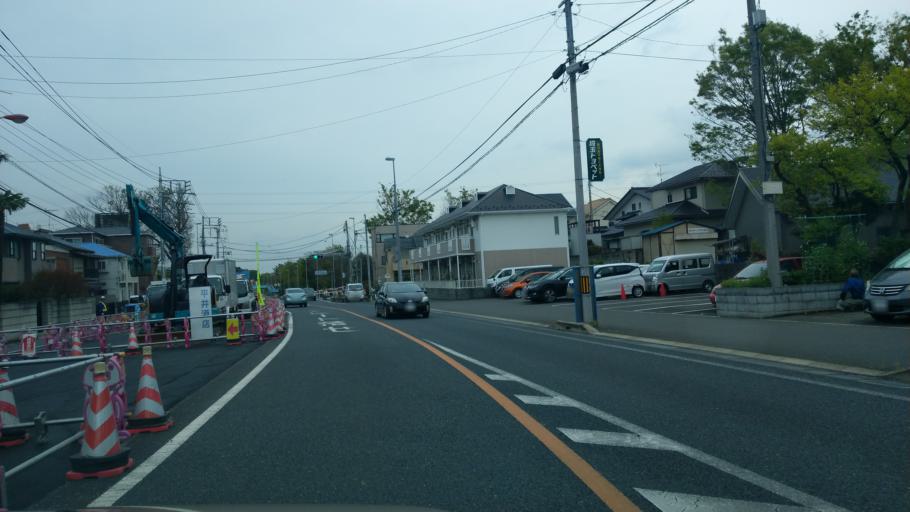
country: JP
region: Saitama
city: Saitama
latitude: 35.9138
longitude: 139.6382
